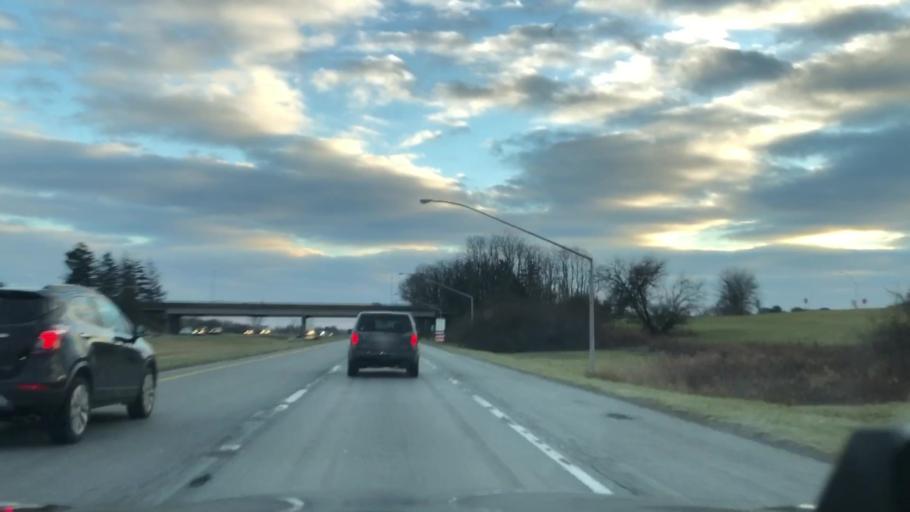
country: US
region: Pennsylvania
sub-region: Northampton County
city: Palmer Heights
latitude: 40.6990
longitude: -75.2897
